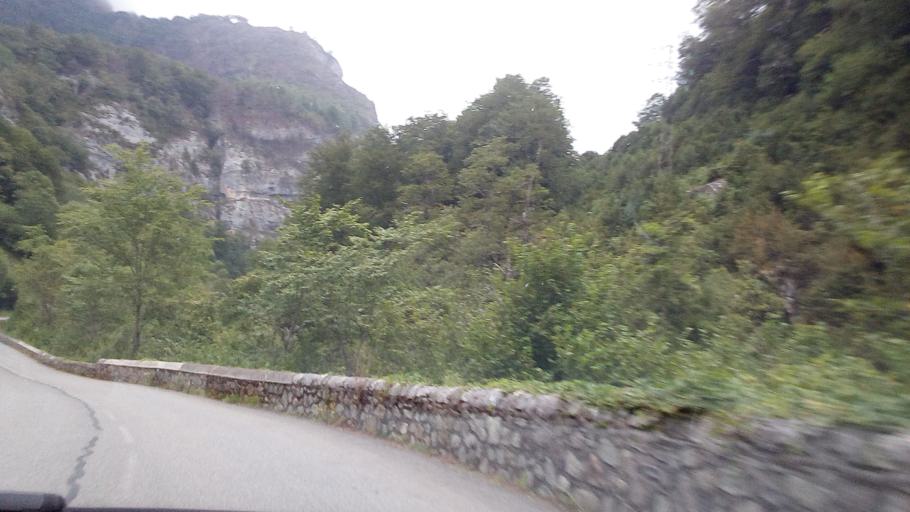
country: FR
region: Aquitaine
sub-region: Departement des Pyrenees-Atlantiques
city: Laruns
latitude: 42.9456
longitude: -0.4423
